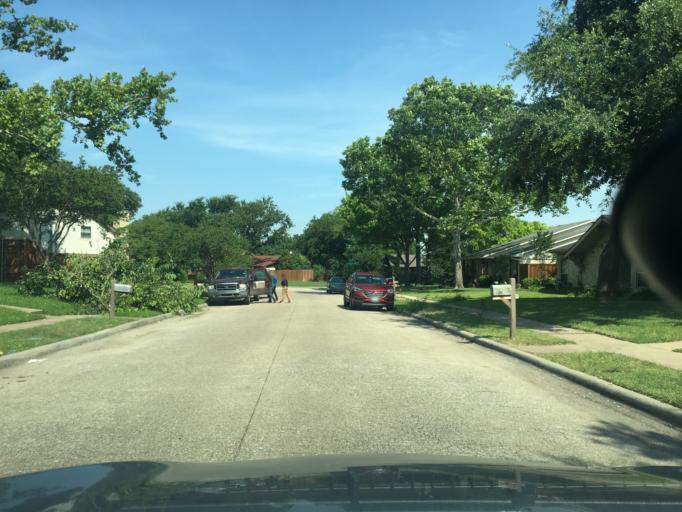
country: US
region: Texas
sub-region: Dallas County
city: Richardson
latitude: 32.9627
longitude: -96.6778
